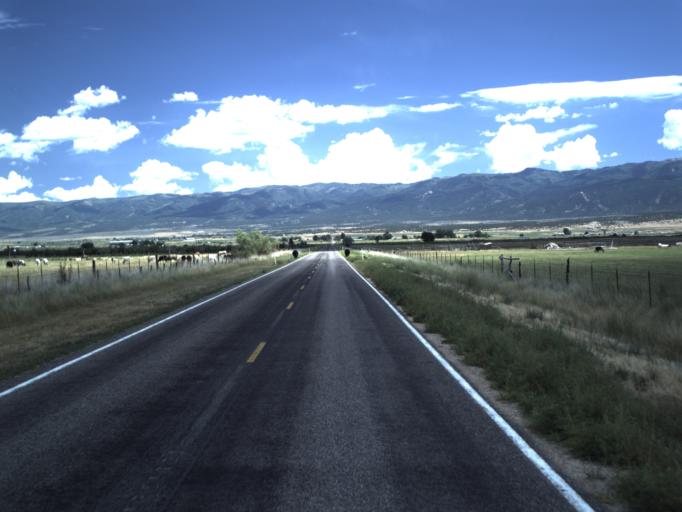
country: US
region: Utah
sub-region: Sanpete County
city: Moroni
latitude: 39.4755
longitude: -111.6075
